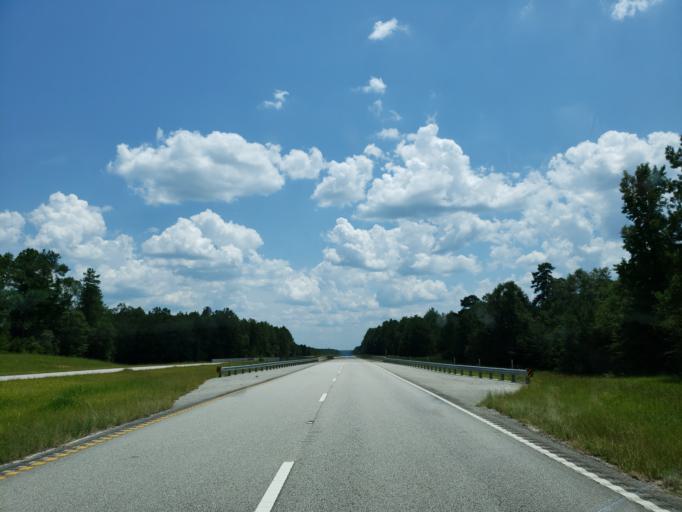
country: US
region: Mississippi
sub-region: Greene County
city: Leakesville
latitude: 31.2067
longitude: -88.5083
